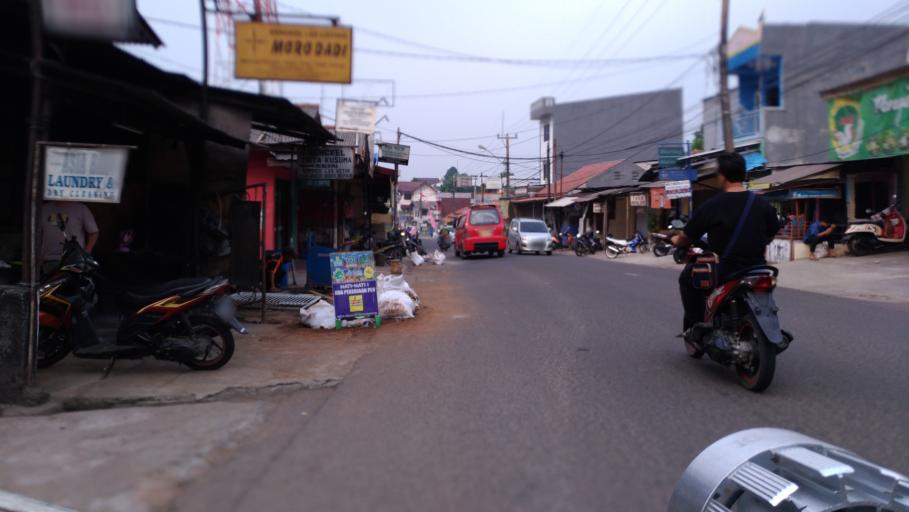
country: ID
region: West Java
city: Depok
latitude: -6.3659
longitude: 106.8601
